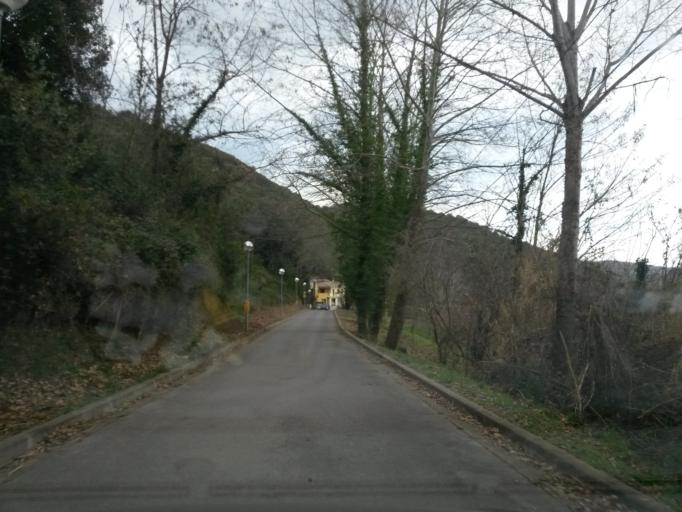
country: ES
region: Catalonia
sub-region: Provincia de Girona
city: Angles
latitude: 41.9665
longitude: 2.6458
